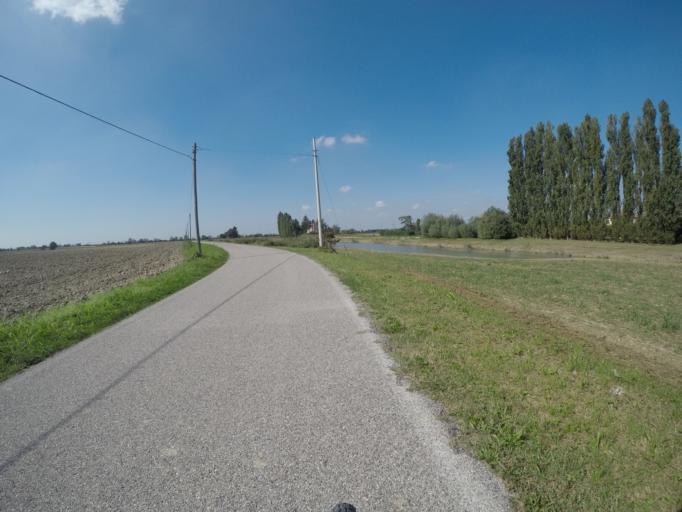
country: IT
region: Veneto
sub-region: Provincia di Rovigo
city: Polesella
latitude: 44.9790
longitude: 11.7556
